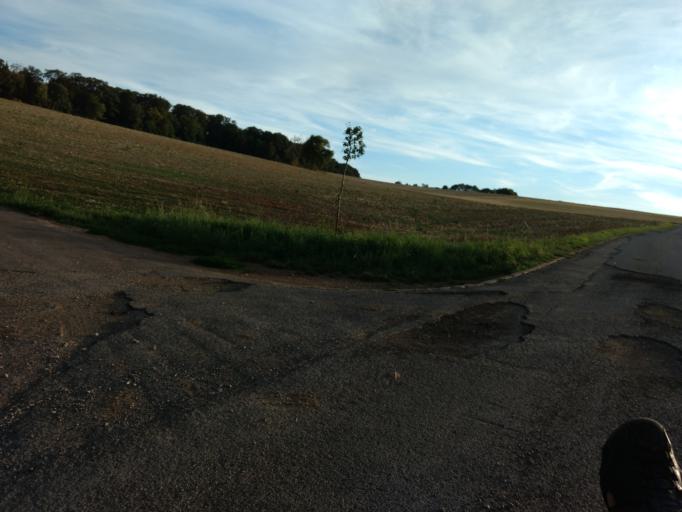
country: DE
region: Saarland
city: Merzig
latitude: 49.4061
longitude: 6.6130
